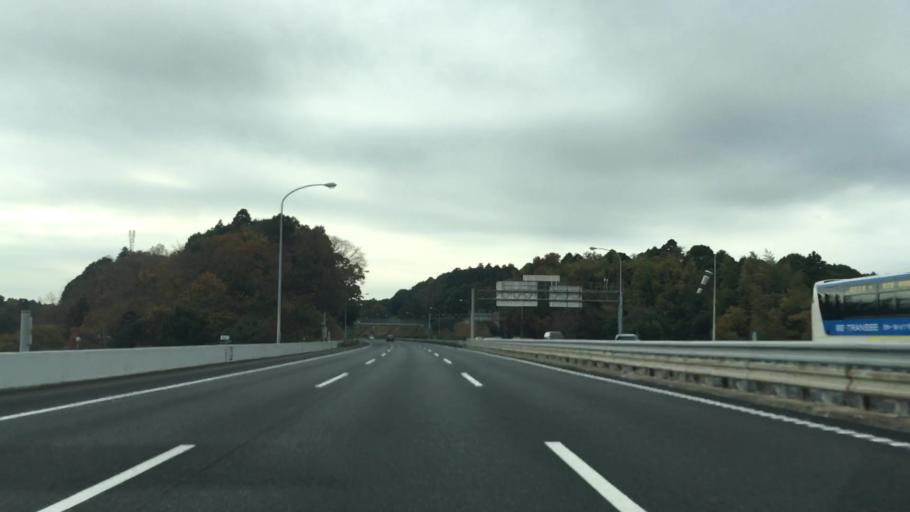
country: JP
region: Chiba
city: Narita
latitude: 35.7665
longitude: 140.3282
